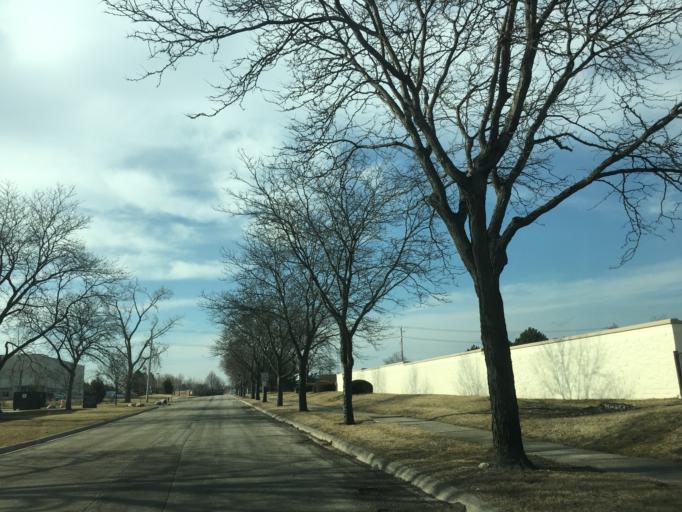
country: US
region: Illinois
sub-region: Cook County
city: Hoffman Estates
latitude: 42.0725
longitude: -88.0617
